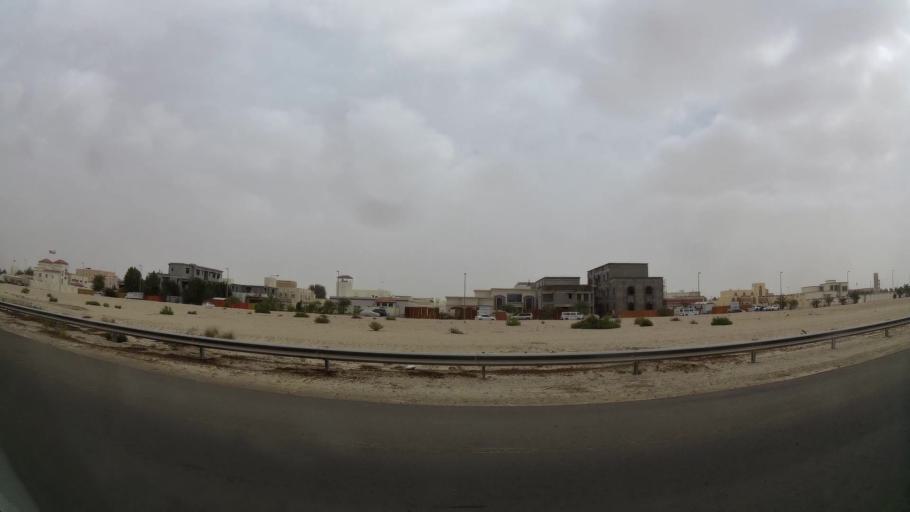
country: AE
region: Abu Dhabi
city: Abu Dhabi
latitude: 24.3939
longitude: 54.7180
